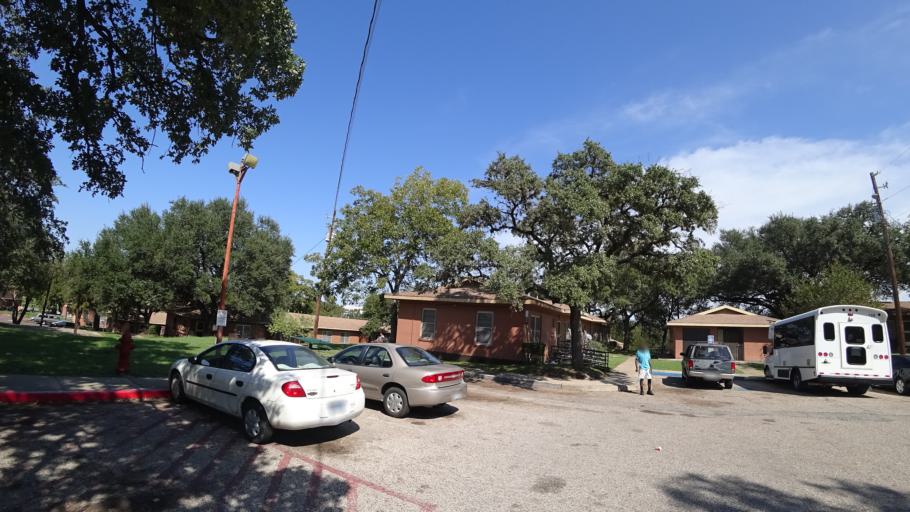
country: US
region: Texas
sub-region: Travis County
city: Austin
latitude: 30.2684
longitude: -97.7185
